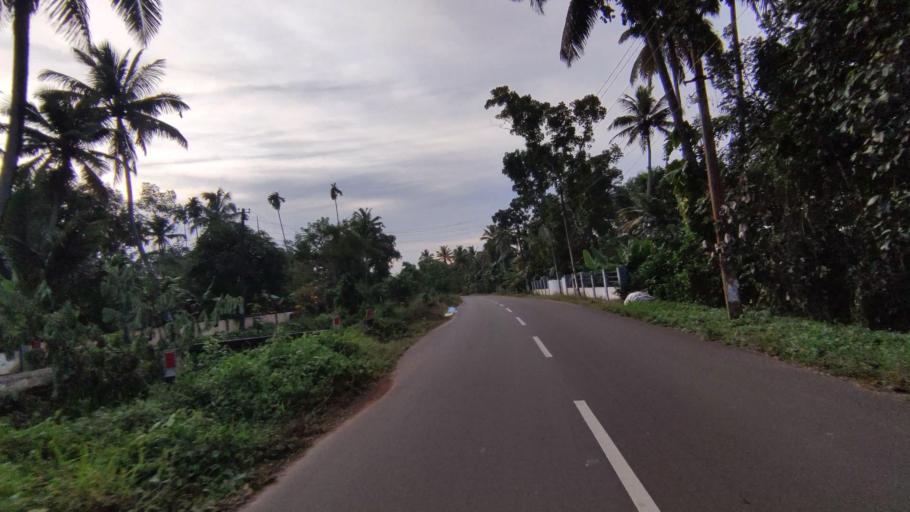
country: IN
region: Kerala
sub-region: Kottayam
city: Kottayam
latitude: 9.6437
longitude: 76.4840
